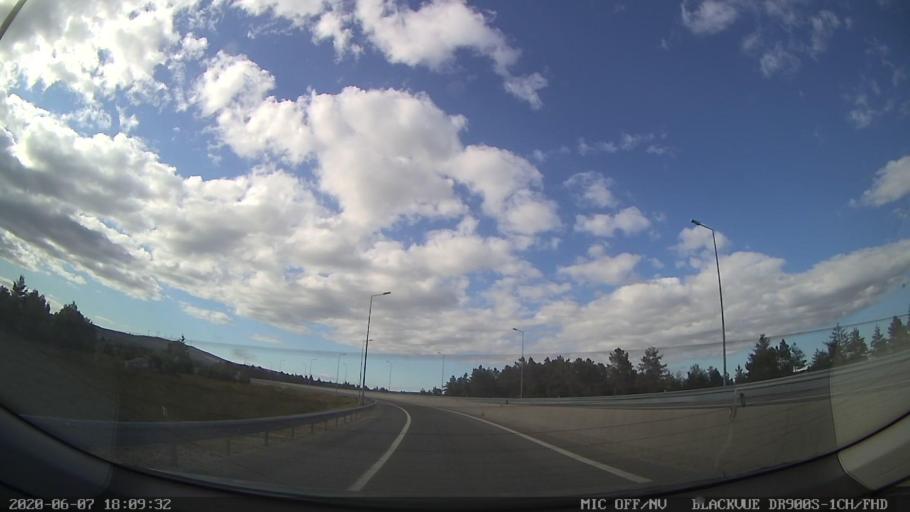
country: PT
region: Vila Real
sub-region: Vila Pouca de Aguiar
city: Vila Pouca de Aguiar
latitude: 41.5056
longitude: -7.6542
